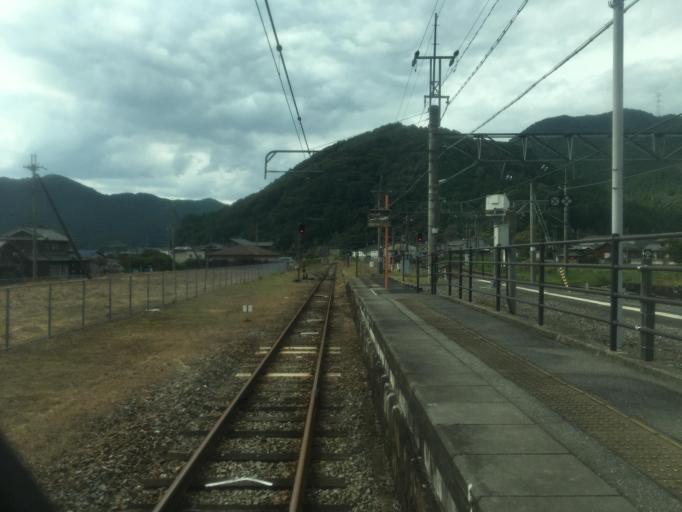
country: JP
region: Hyogo
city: Nishiwaki
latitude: 35.0828
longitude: 135.0493
